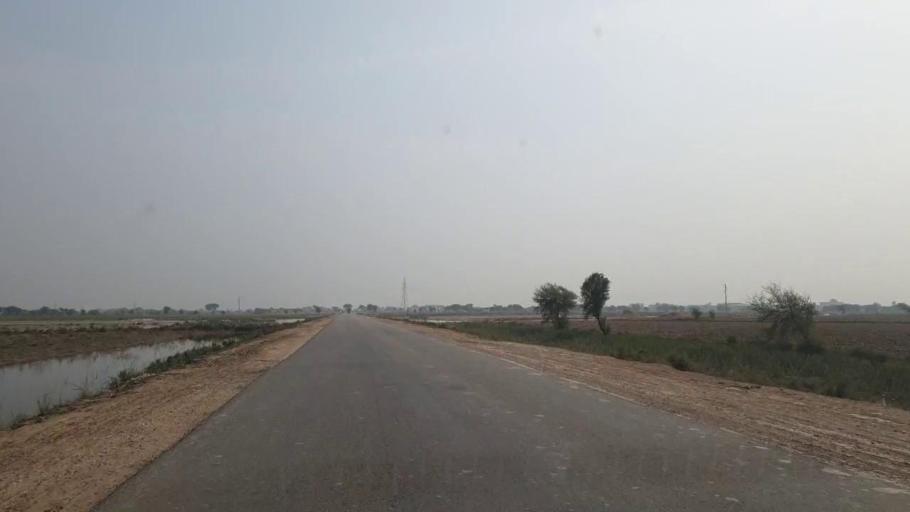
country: PK
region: Sindh
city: Matli
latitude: 25.0591
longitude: 68.6701
